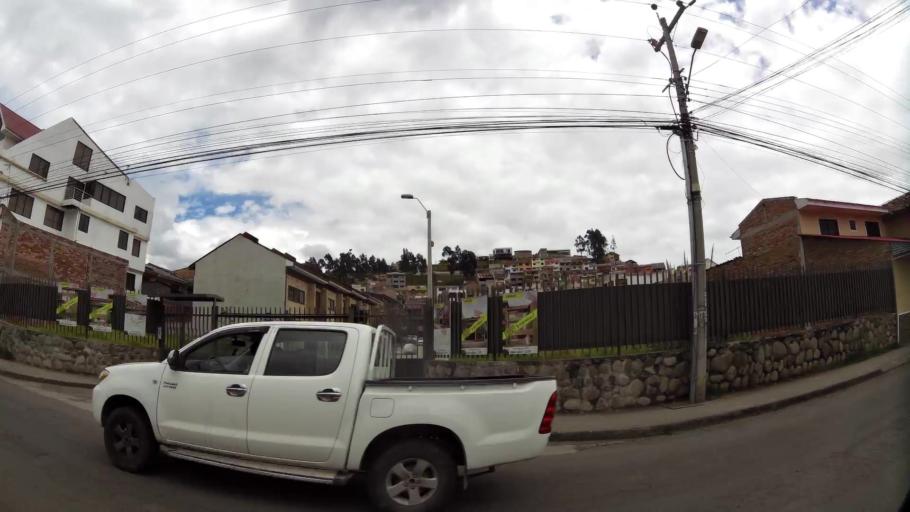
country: EC
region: Azuay
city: Cuenca
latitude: -2.8885
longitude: -79.0268
